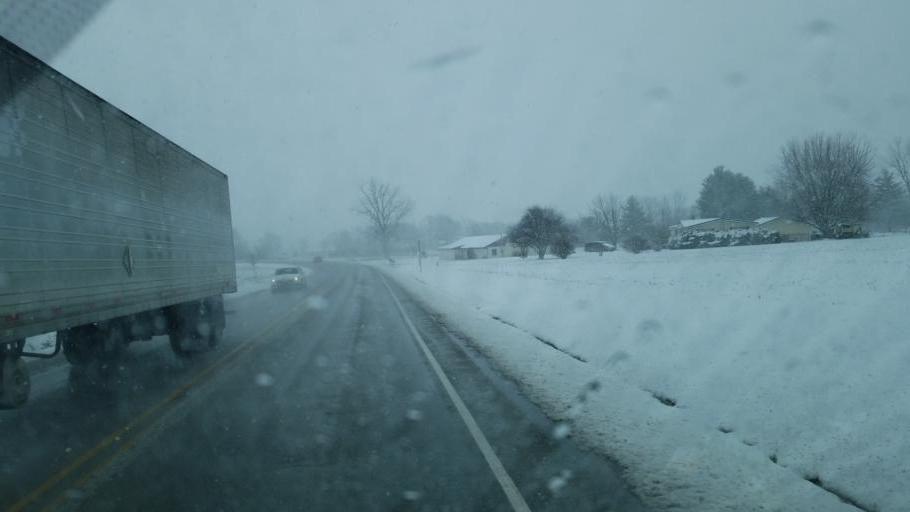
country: US
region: Indiana
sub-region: Wayne County
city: Hagerstown
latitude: 40.0209
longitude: -85.1868
